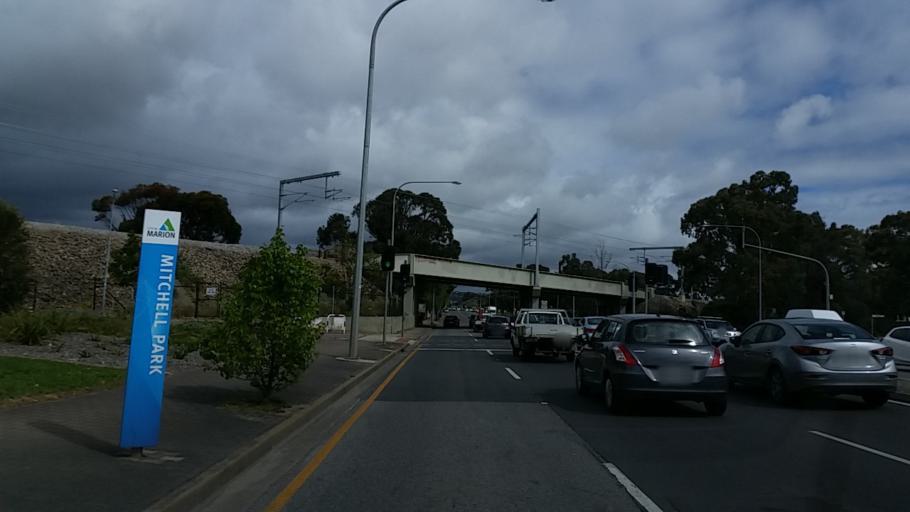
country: AU
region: South Australia
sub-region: Marion
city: Clovelly Park
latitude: -34.9945
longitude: 138.5571
